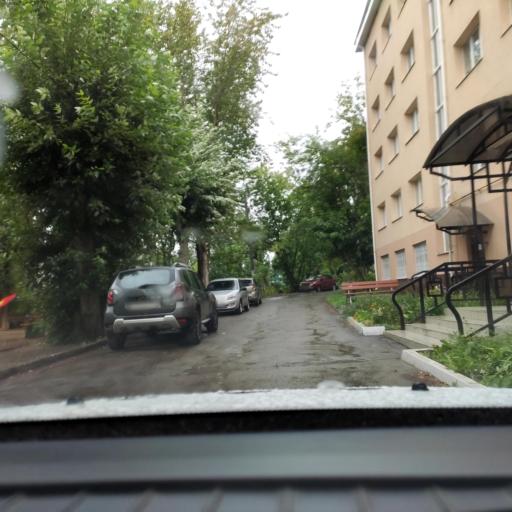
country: RU
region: Perm
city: Perm
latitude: 58.1157
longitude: 56.2988
